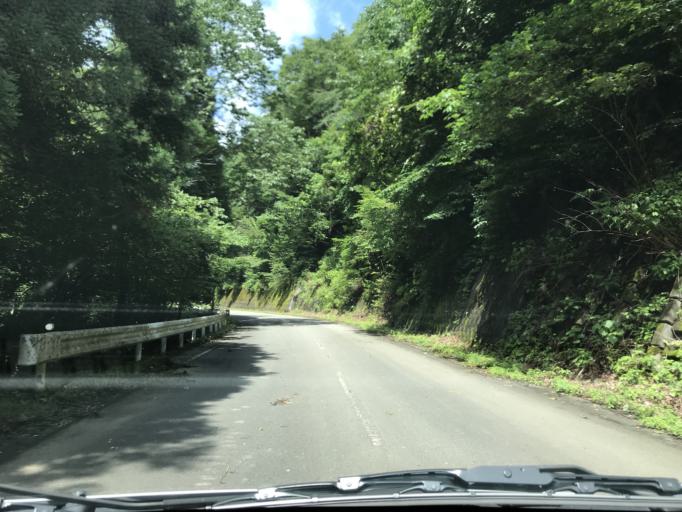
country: JP
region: Iwate
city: Tono
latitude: 39.0754
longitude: 141.4093
